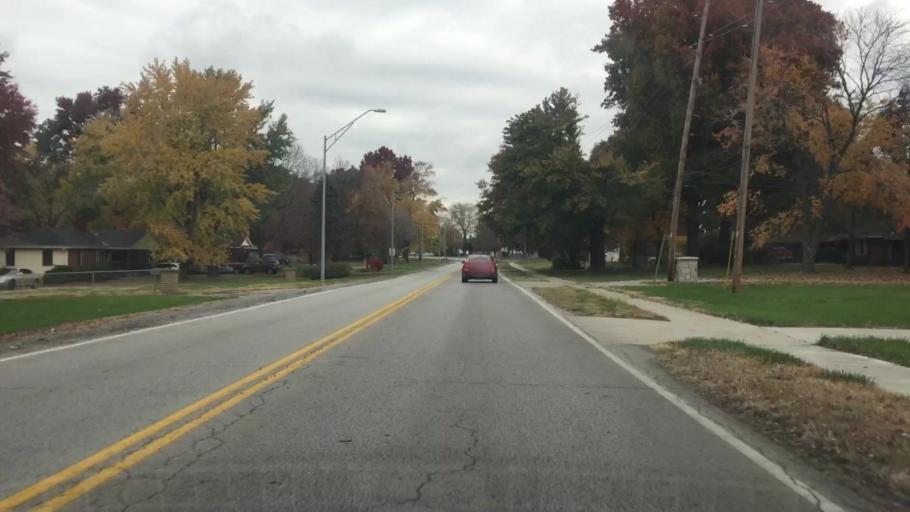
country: US
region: Missouri
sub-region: Jackson County
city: Raytown
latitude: 39.0395
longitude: -94.4371
